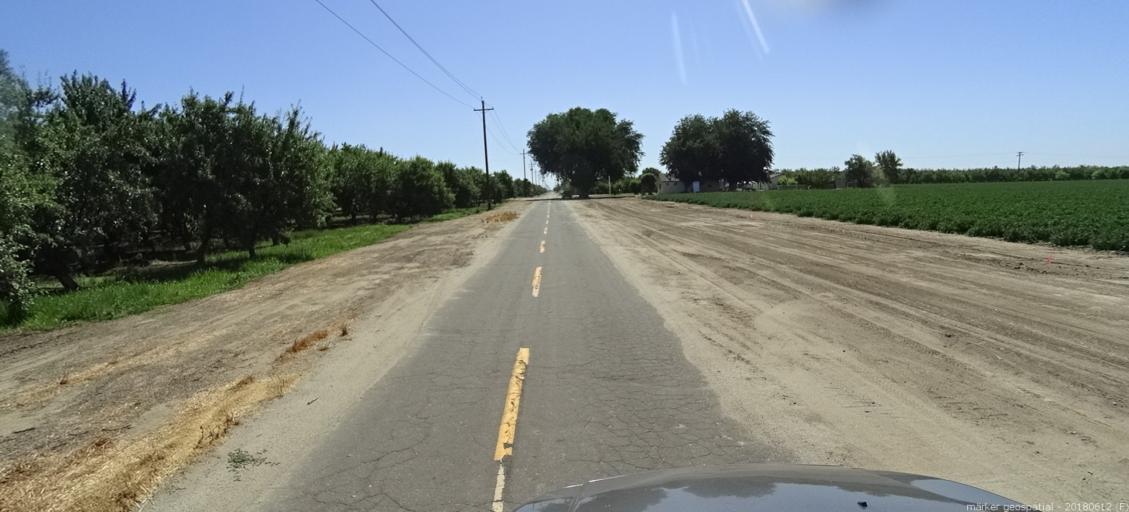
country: US
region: California
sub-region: Madera County
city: Chowchilla
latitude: 37.0325
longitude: -120.3667
